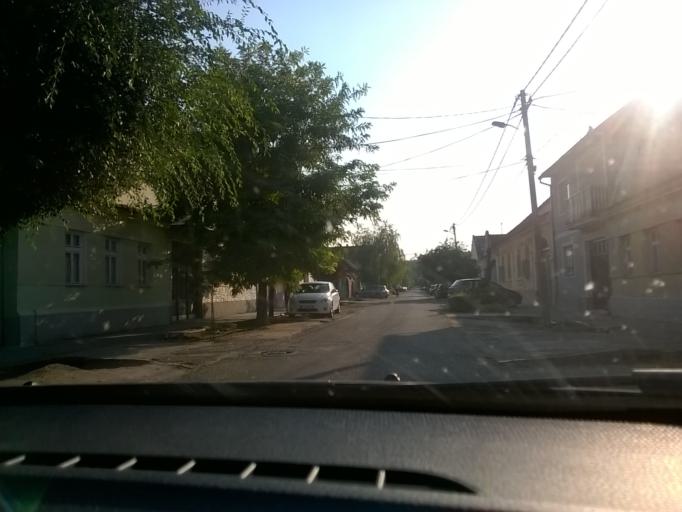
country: RS
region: Autonomna Pokrajina Vojvodina
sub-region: Juznobanatski Okrug
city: Vrsac
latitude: 45.1199
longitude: 21.2887
